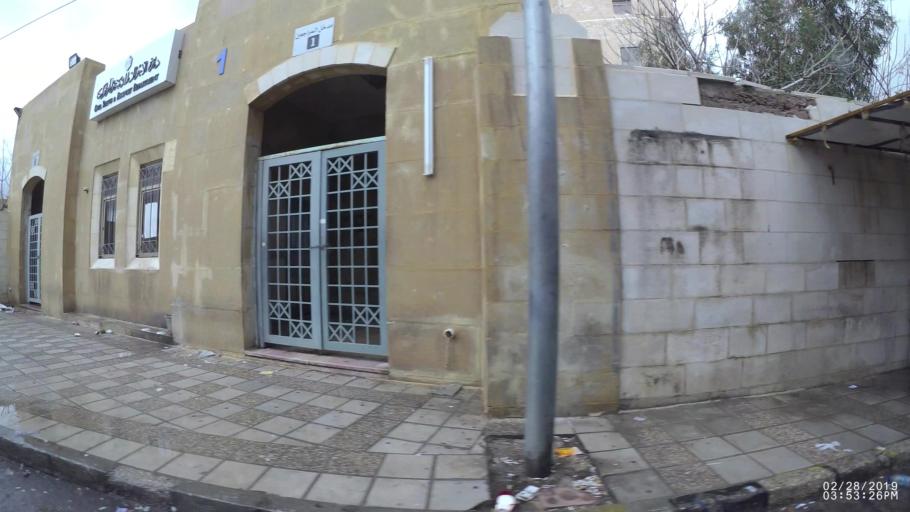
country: JO
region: Amman
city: Amman
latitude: 31.9944
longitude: 35.9267
